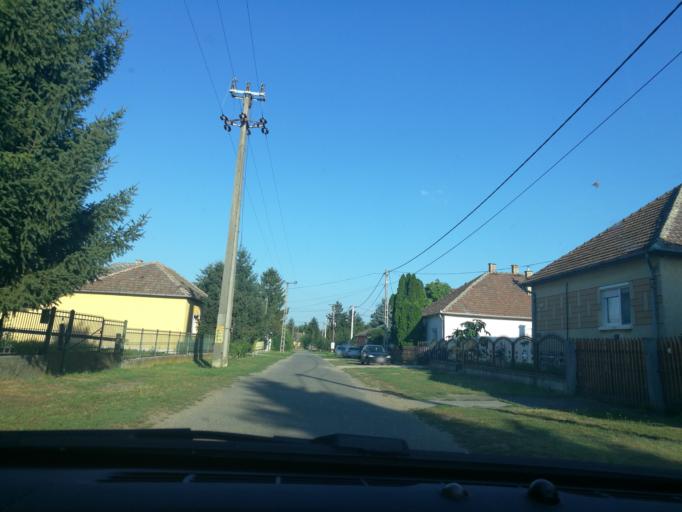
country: HU
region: Szabolcs-Szatmar-Bereg
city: Tiszabercel
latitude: 48.1623
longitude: 21.5978
